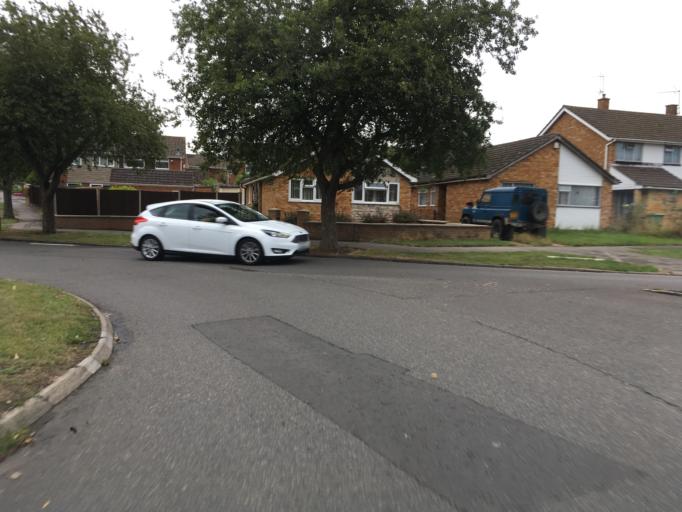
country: GB
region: England
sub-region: Buckinghamshire
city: Bletchley
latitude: 52.0074
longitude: -0.7461
